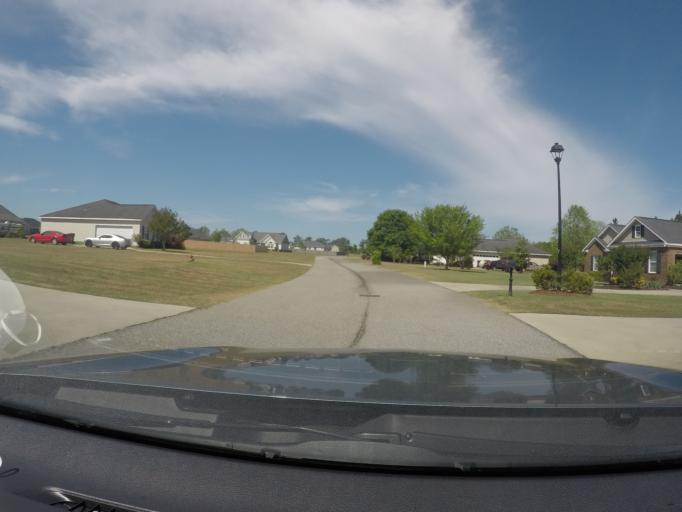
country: US
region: Georgia
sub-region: Bulloch County
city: Statesboro
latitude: 32.3601
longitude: -81.7546
